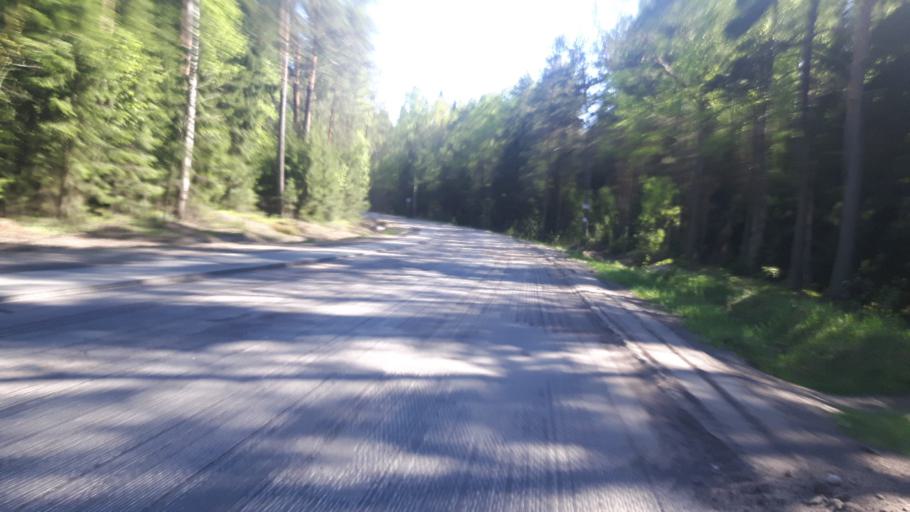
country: RU
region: Leningrad
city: Sosnovyy Bor
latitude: 60.2295
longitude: 29.0021
